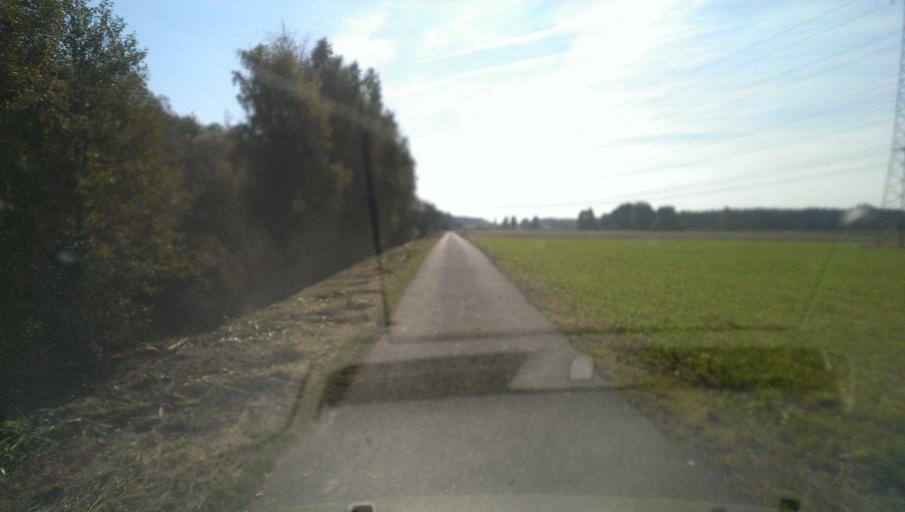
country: DE
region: Brandenburg
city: Am Mellensee
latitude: 52.2053
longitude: 13.3386
